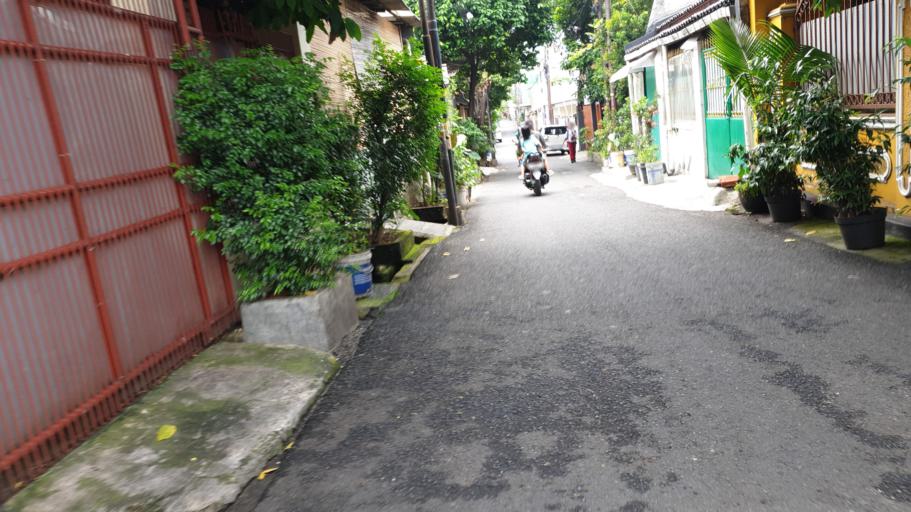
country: ID
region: Jakarta Raya
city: Jakarta
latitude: -6.2614
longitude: 106.7933
